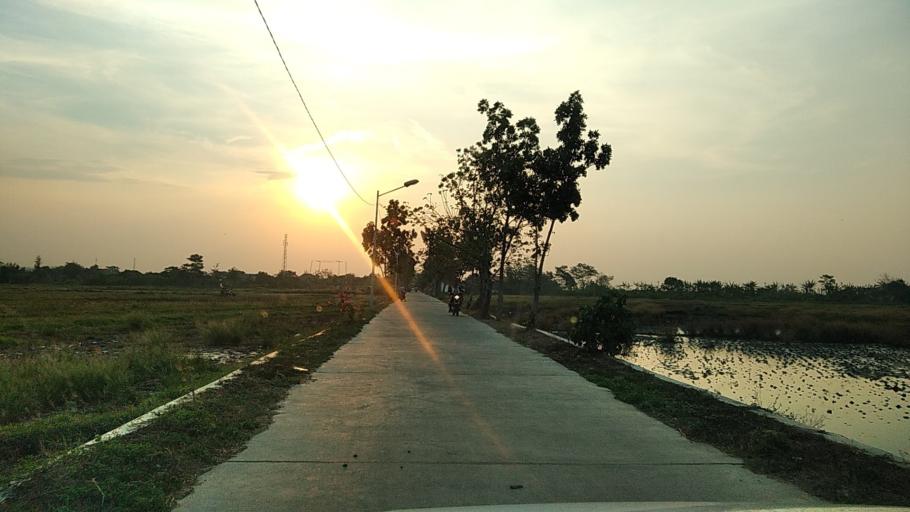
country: ID
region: Central Java
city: Semarang
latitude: -6.9588
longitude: 110.3070
